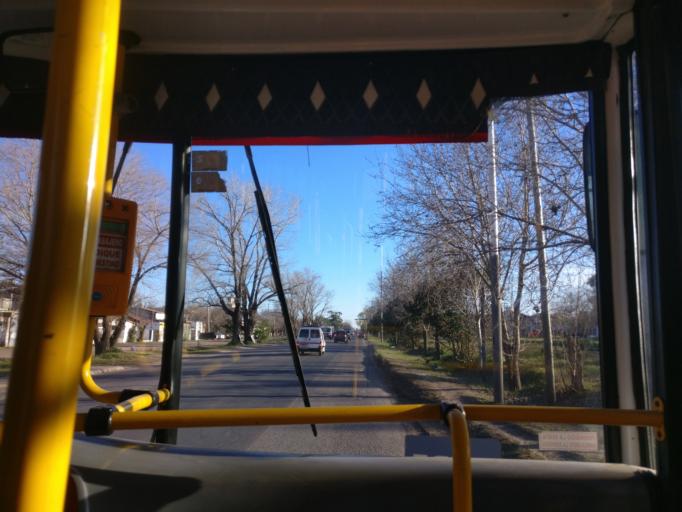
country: AR
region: Buenos Aires
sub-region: Partido de Ezeiza
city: Ezeiza
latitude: -34.9081
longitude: -58.5914
